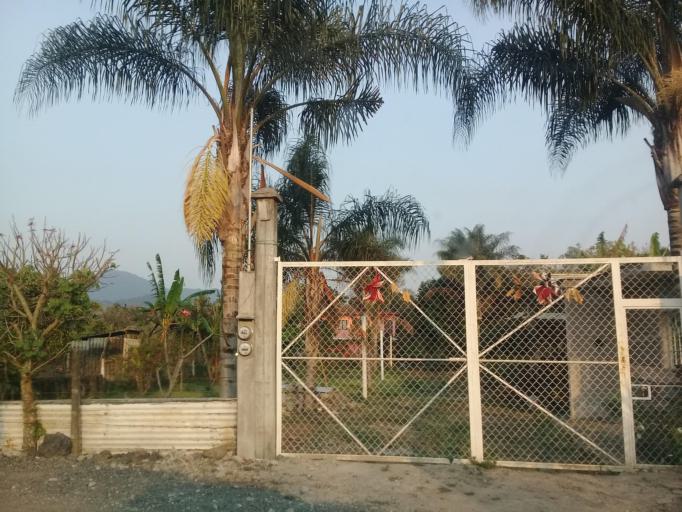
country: MX
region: Veracruz
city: Ixtac Zoquitlan
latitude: 18.8470
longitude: -97.0560
